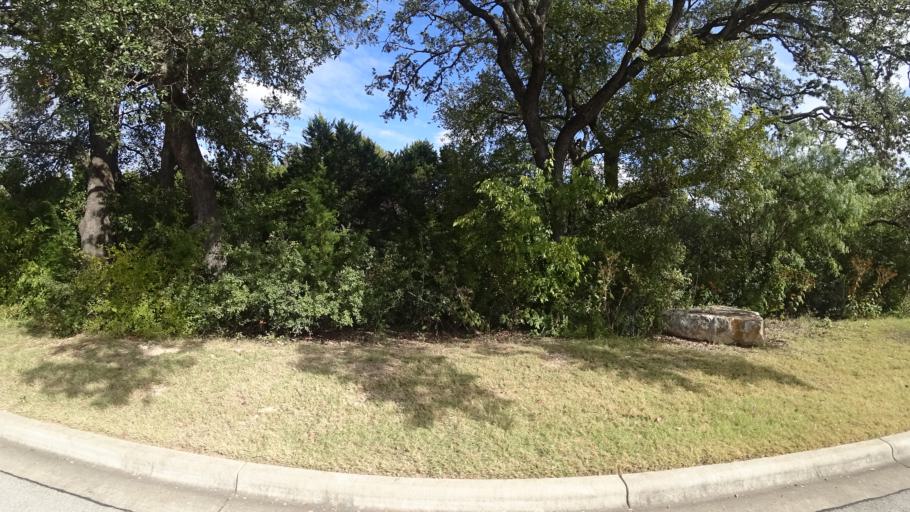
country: US
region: Texas
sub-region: Travis County
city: Hudson Bend
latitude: 30.3673
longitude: -97.9057
